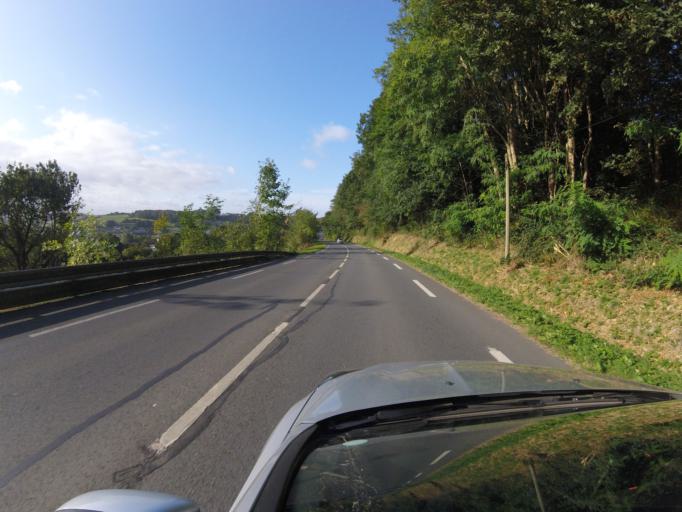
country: FR
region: Haute-Normandie
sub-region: Departement de la Seine-Maritime
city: Fecamp
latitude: 49.7610
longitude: 0.3947
